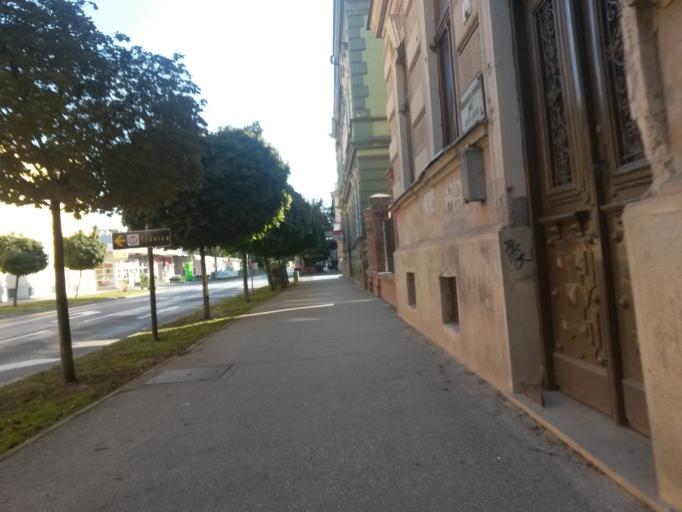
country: HR
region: Osjecko-Baranjska
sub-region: Grad Osijek
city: Osijek
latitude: 45.5598
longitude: 18.6824
